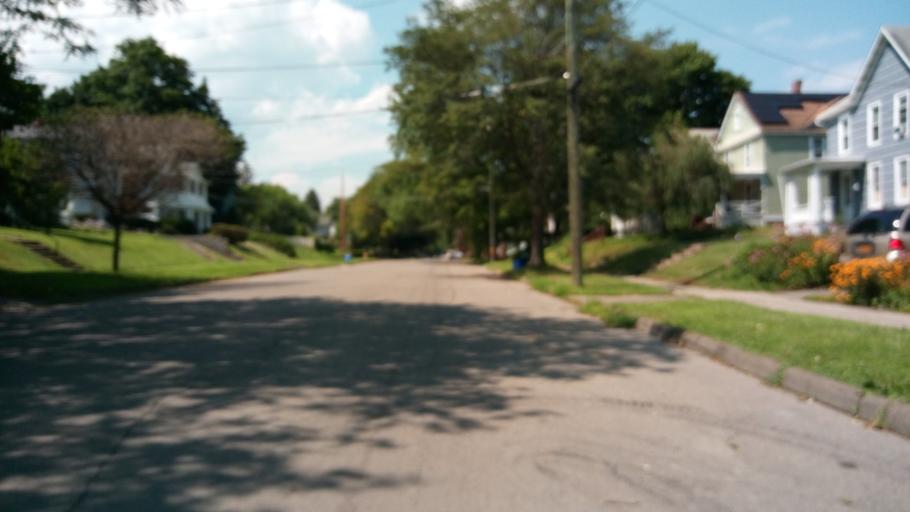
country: US
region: New York
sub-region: Chemung County
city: Elmira
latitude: 42.0885
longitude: -76.8208
